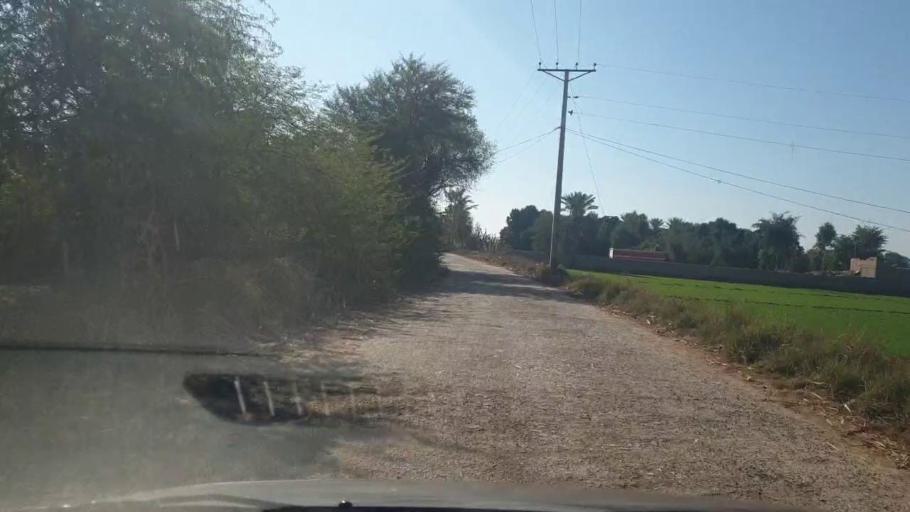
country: PK
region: Sindh
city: Bozdar
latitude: 27.2599
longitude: 68.6527
